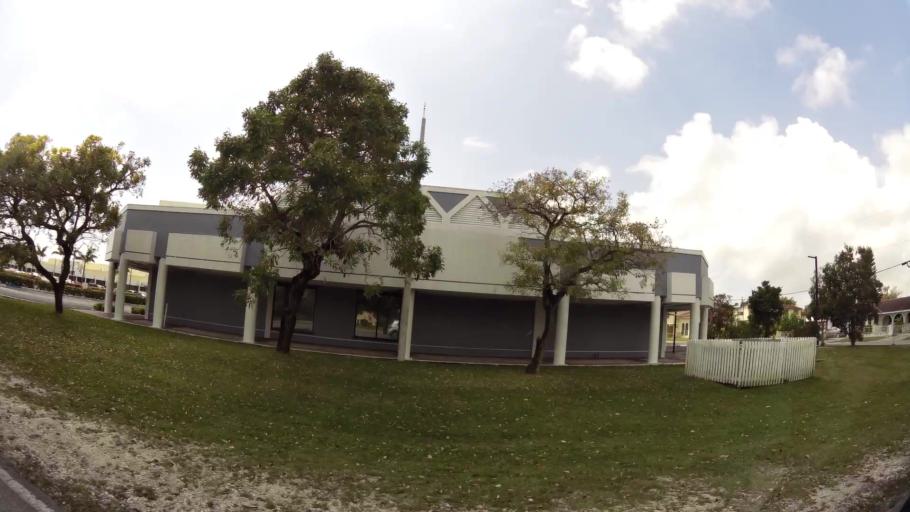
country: BS
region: Freeport
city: Lucaya
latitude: 26.5219
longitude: -78.6573
